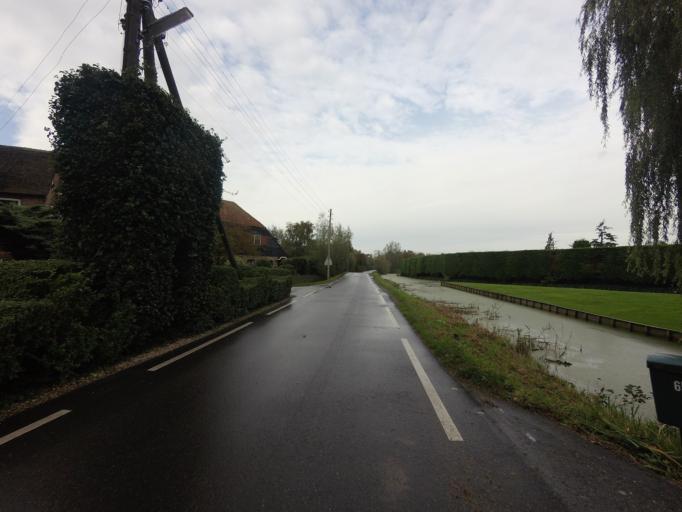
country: NL
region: South Holland
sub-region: Molenwaard
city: Liesveld
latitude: 51.9466
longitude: 4.8145
